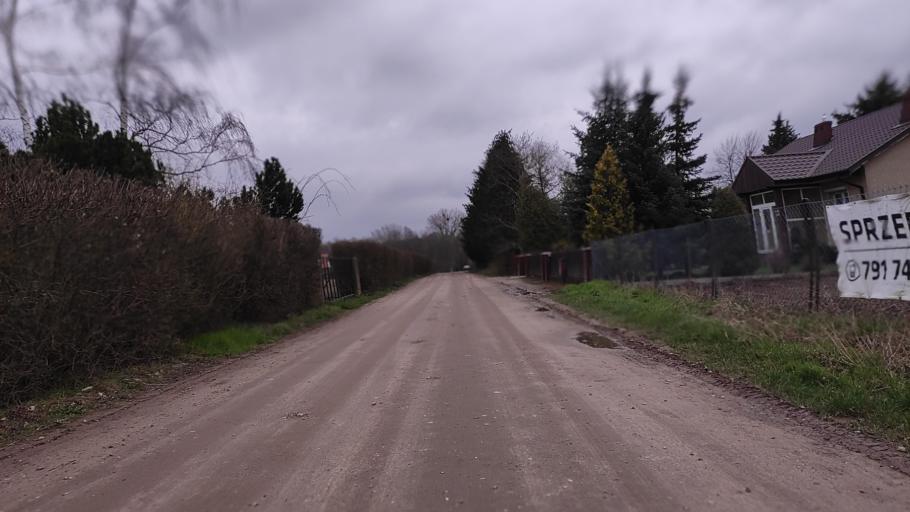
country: PL
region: Greater Poland Voivodeship
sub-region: Powiat poznanski
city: Kostrzyn
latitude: 52.4057
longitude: 17.1700
